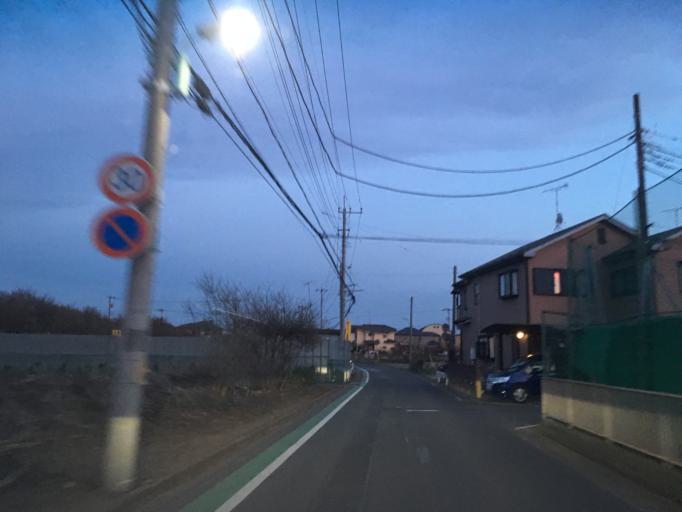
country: JP
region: Saitama
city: Sayama
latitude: 35.8009
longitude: 139.4026
